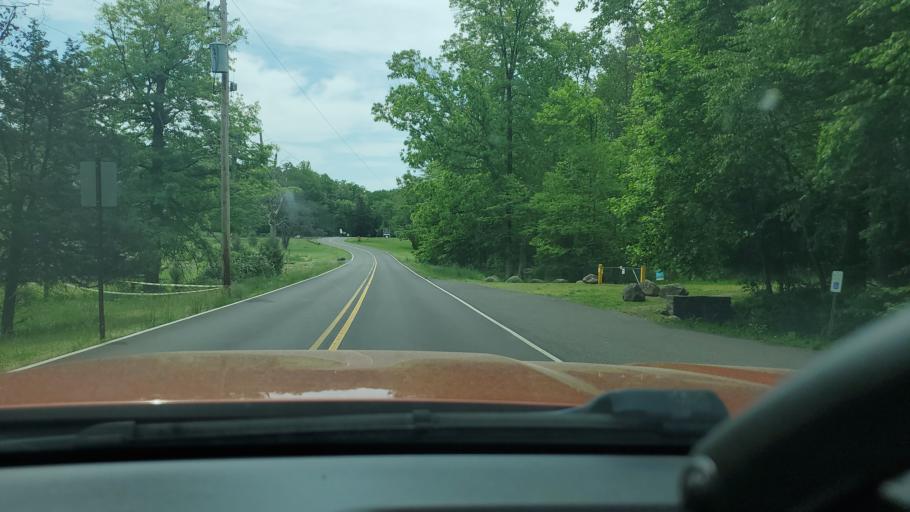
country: US
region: Pennsylvania
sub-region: Montgomery County
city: Red Hill
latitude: 40.3323
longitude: -75.4879
